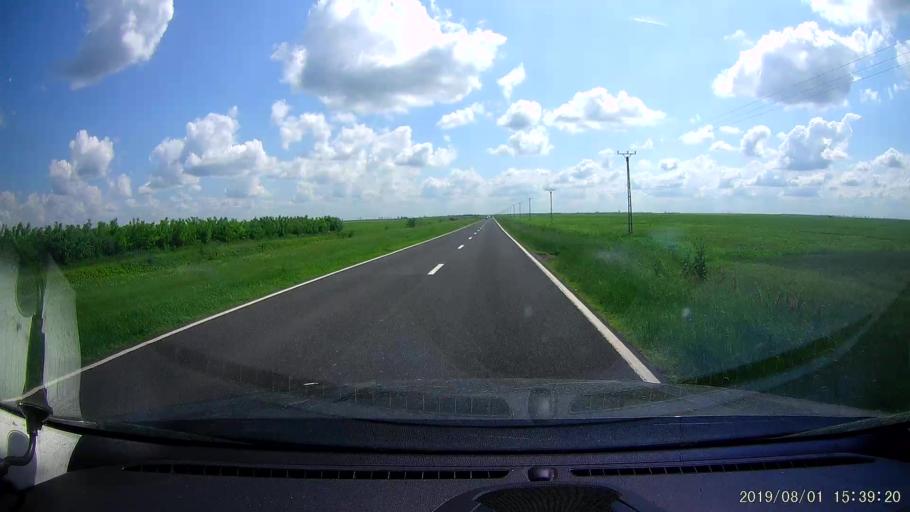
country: RO
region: Braila
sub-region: Comuna Insuratei
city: Insuratei
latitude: 44.8602
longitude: 27.5618
